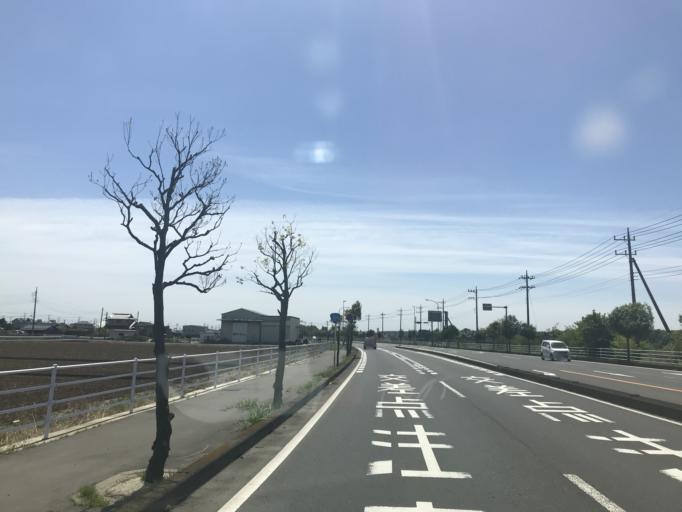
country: JP
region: Ibaraki
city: Shimodate
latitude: 36.2893
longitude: 139.9707
